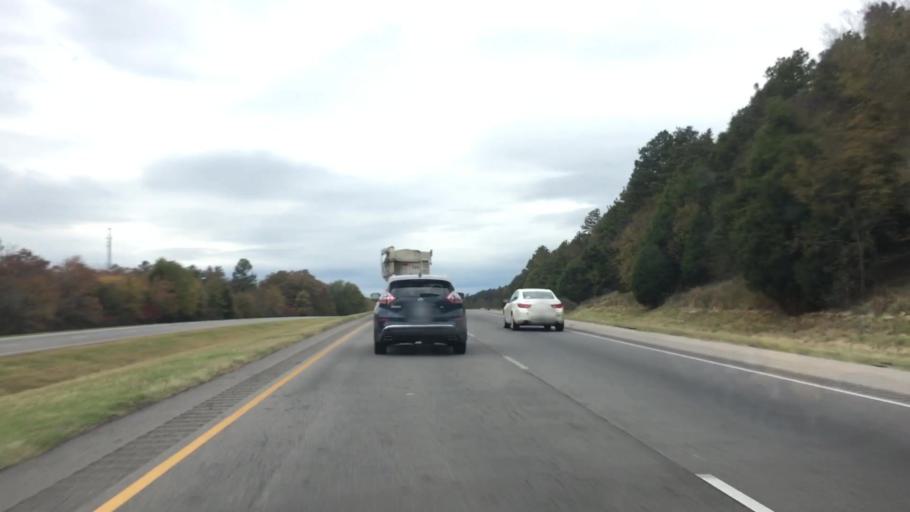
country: US
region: Arkansas
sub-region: Johnson County
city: Coal Hill
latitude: 35.5005
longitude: -93.7213
